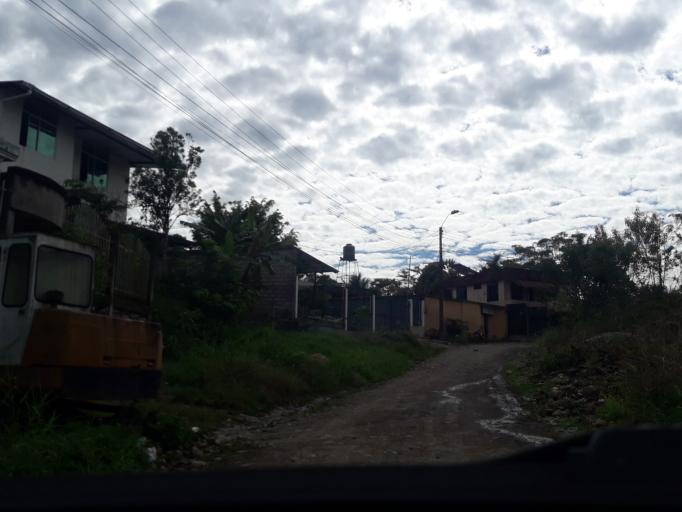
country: EC
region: Napo
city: Tena
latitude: -0.9822
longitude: -77.8225
